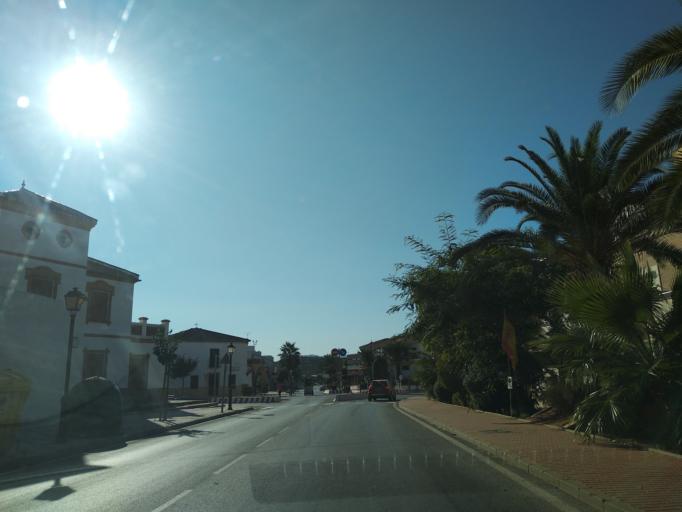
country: ES
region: Andalusia
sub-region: Provincia de Malaga
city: Mollina
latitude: 37.1215
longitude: -4.6597
